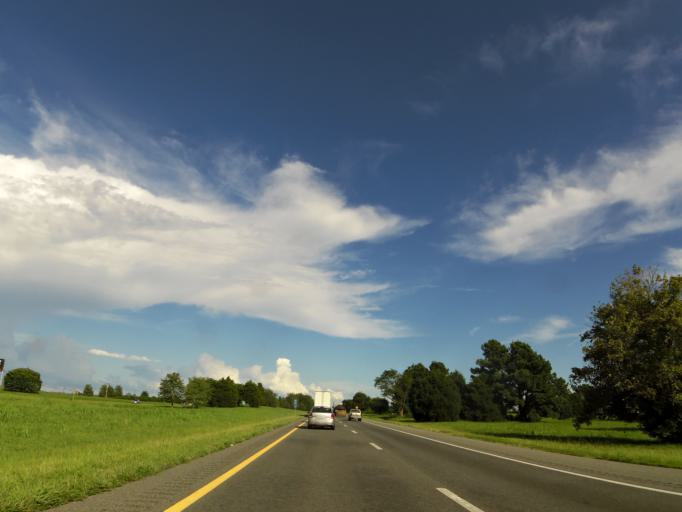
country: US
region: Tennessee
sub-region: Montgomery County
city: Clarksville
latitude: 36.6297
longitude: -87.3167
